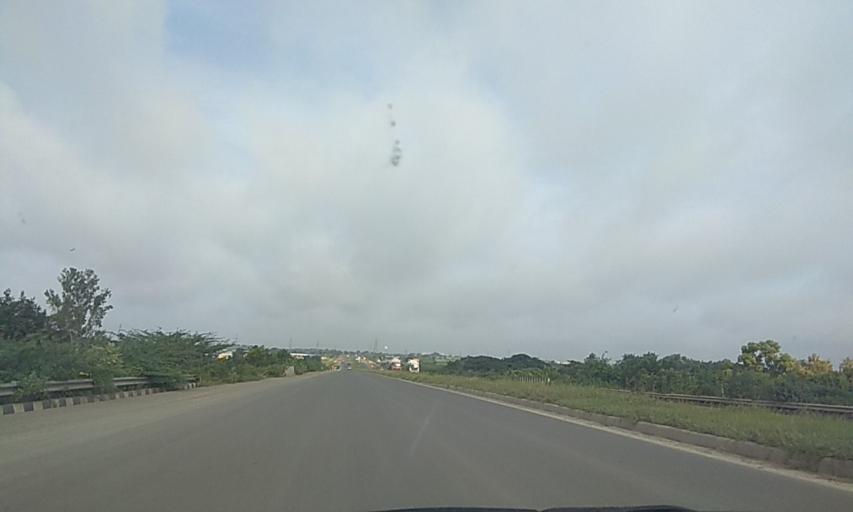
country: IN
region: Karnataka
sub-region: Haveri
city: Haveri
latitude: 14.7744
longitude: 75.4052
